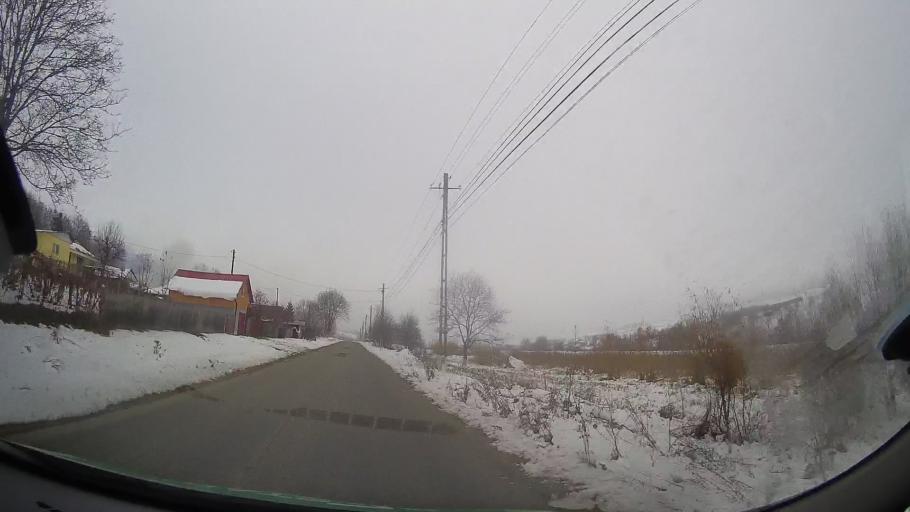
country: RO
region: Bacau
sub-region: Comuna Vultureni
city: Vultureni
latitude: 46.3223
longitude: 27.2924
